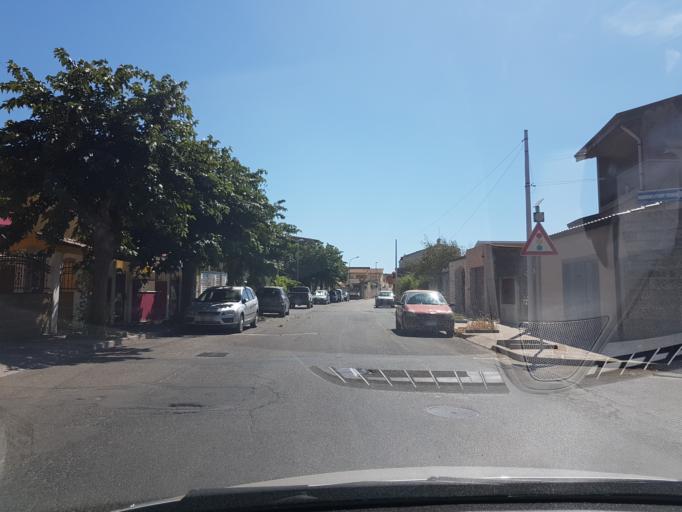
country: IT
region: Sardinia
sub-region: Provincia di Oristano
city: Cabras
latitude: 39.9269
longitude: 8.5369
